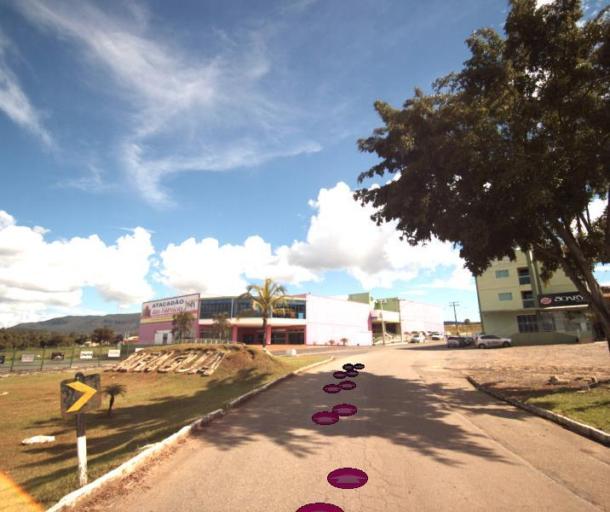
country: BR
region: Goias
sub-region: Jaragua
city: Jaragua
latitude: -15.7590
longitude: -49.3138
